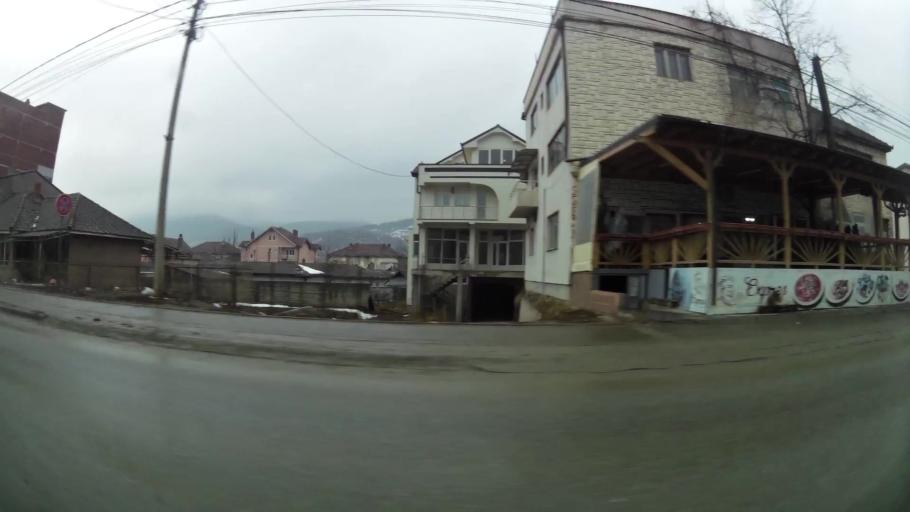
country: XK
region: Ferizaj
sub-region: Hani i Elezit
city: Hani i Elezit
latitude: 42.1519
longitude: 21.2973
